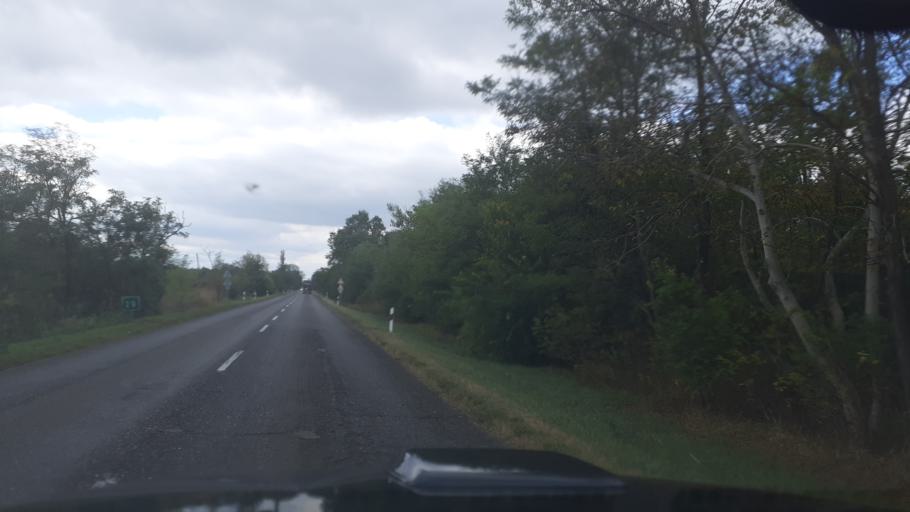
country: HU
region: Bacs-Kiskun
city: Izsak
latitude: 46.8498
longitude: 19.3166
